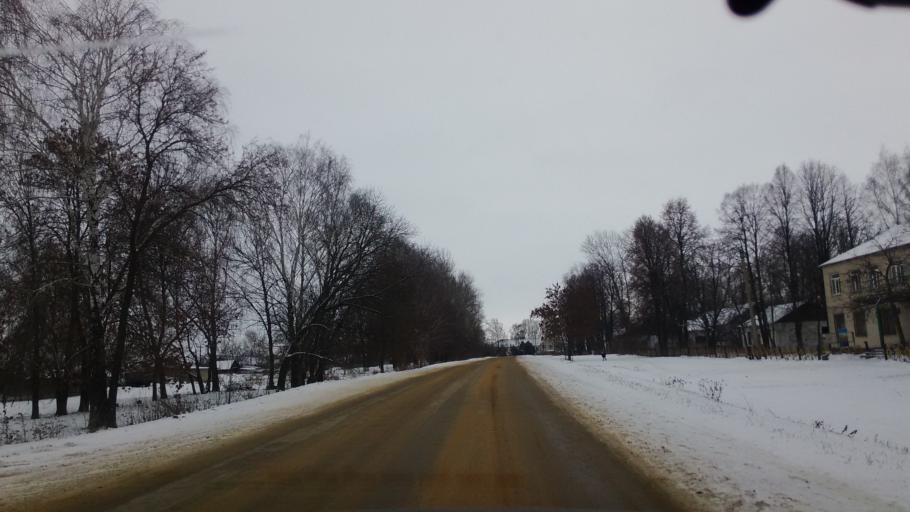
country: RU
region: Tula
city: Bogoroditsk
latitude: 53.7623
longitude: 37.9885
